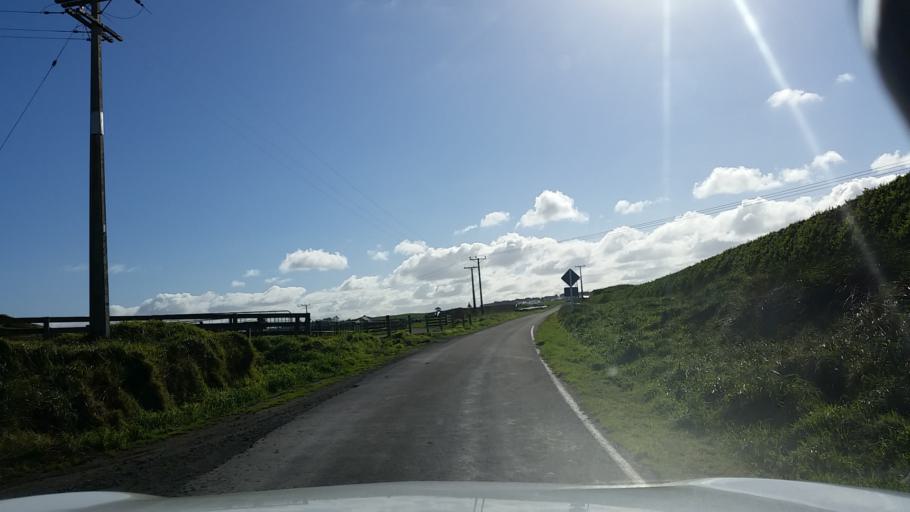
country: NZ
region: Taranaki
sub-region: South Taranaki District
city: Patea
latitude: -39.6829
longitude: 174.3905
